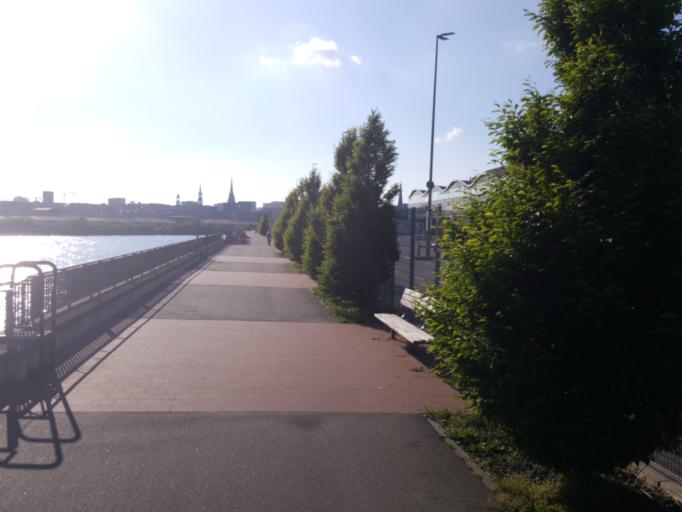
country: DE
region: Hamburg
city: Hamburg-Mitte
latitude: 53.5410
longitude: 10.0180
